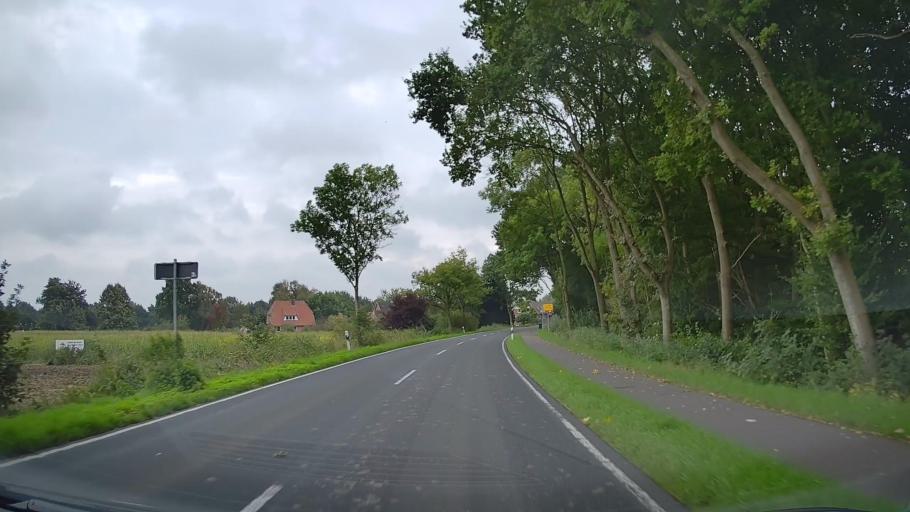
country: DE
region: Lower Saxony
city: Wischhafen
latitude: 53.7967
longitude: 9.3228
